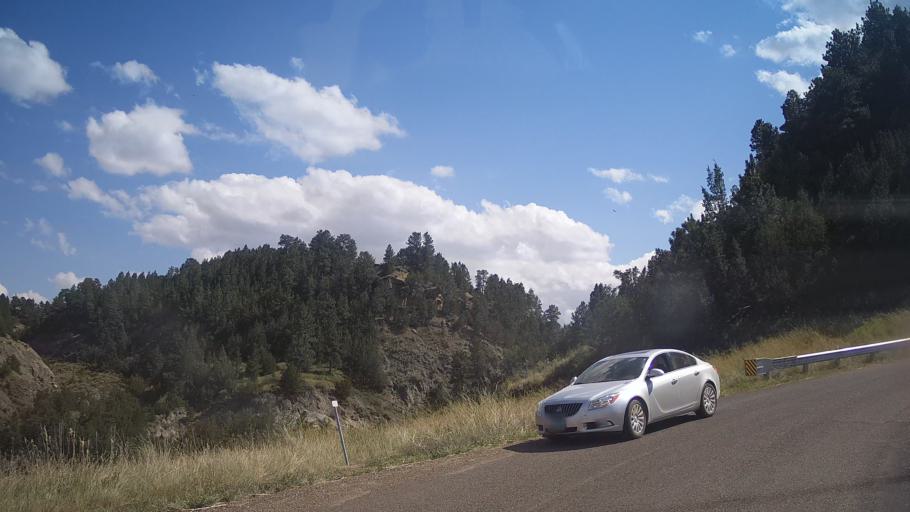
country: US
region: Montana
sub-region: Dawson County
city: Glendive
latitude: 47.0622
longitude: -104.6797
